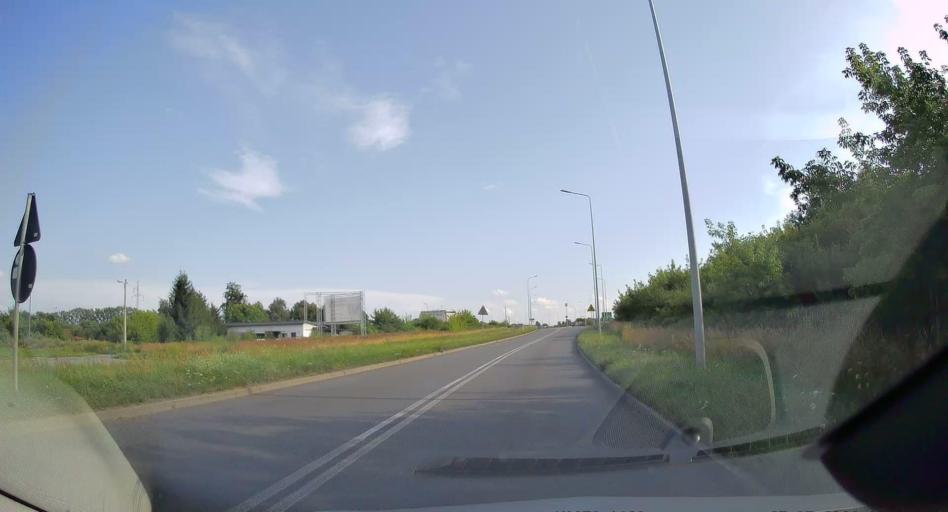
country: PL
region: Swietokrzyskie
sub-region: Powiat konecki
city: Konskie
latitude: 51.2029
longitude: 20.4003
